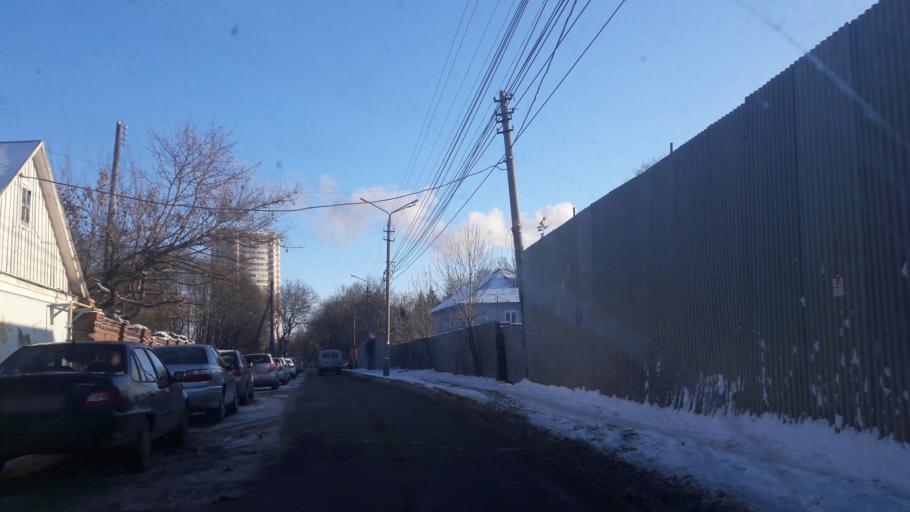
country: RU
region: Tula
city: Tula
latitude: 54.1765
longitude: 37.6078
